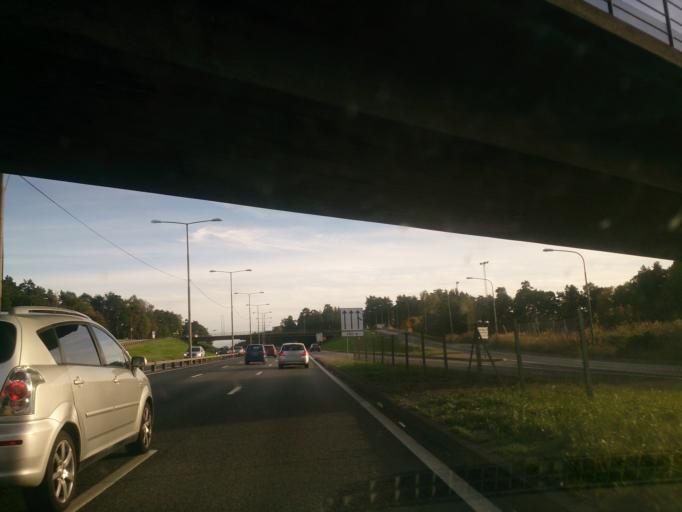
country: SE
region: Stockholm
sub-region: Stockholms Kommun
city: Arsta
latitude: 59.2750
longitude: 18.0929
